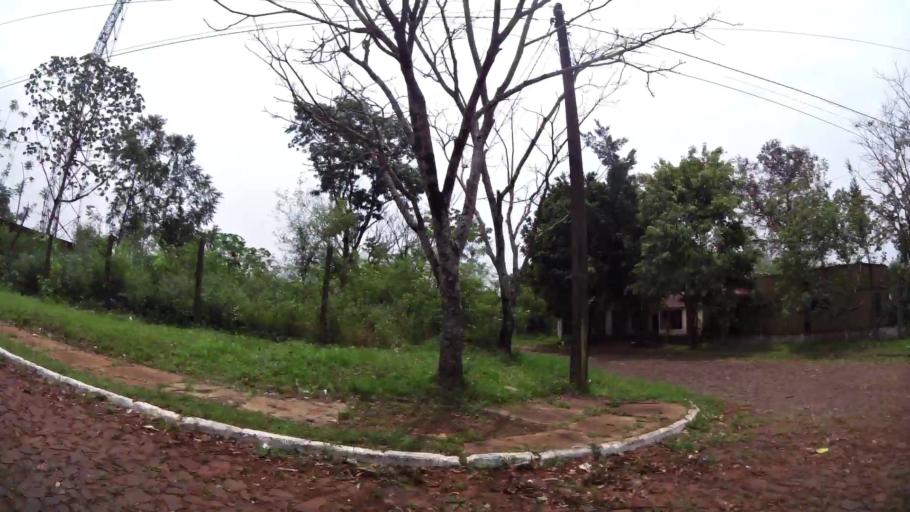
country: PY
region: Alto Parana
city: Presidente Franco
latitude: -25.5514
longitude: -54.6128
